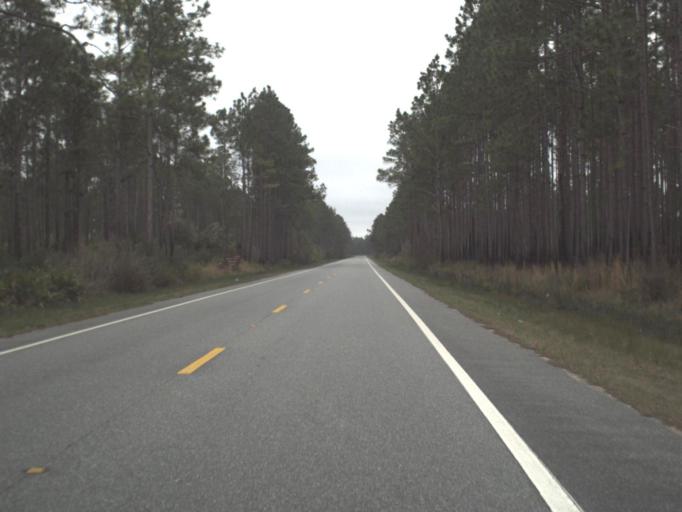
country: US
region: Florida
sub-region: Franklin County
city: Apalachicola
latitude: 29.9057
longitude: -84.9778
